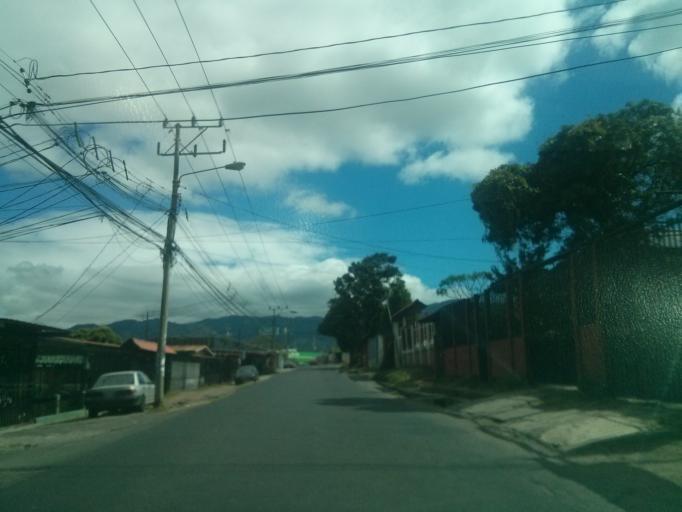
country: CR
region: San Jose
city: San Juan de Dios
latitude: 9.8898
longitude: -84.0795
